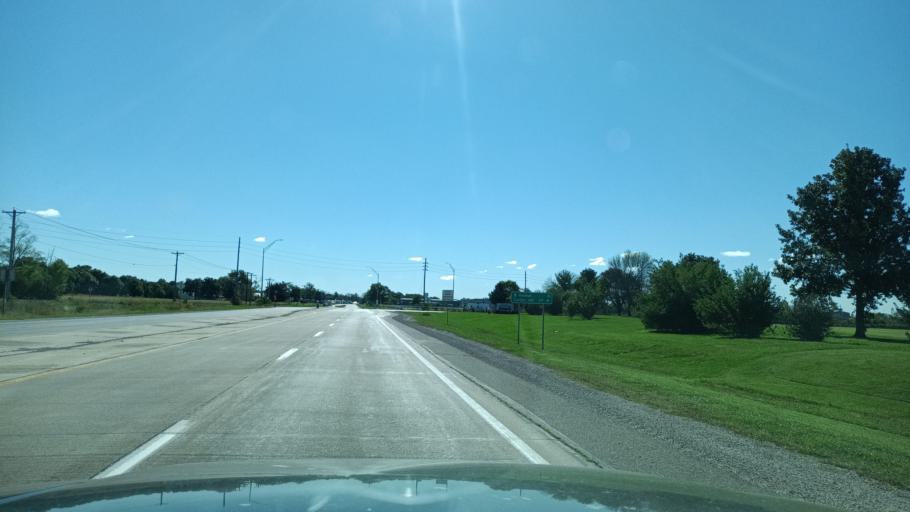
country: US
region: Iowa
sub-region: Lee County
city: Keokuk
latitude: 40.4375
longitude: -91.4276
